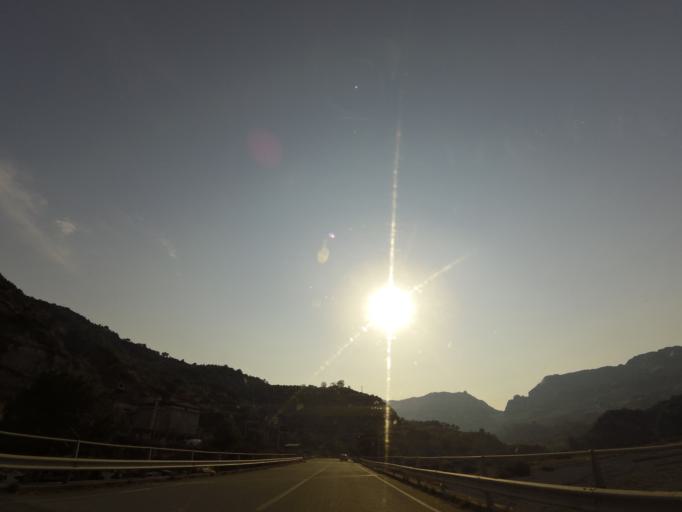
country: IT
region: Calabria
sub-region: Provincia di Reggio Calabria
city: Stilo
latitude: 38.4657
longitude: 16.4909
